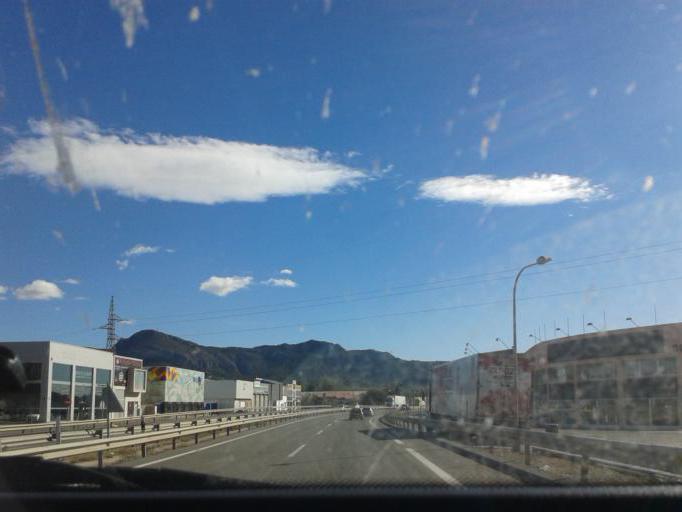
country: ES
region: Valencia
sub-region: Provincia de Alicante
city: Villena
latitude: 38.6183
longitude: -0.8488
